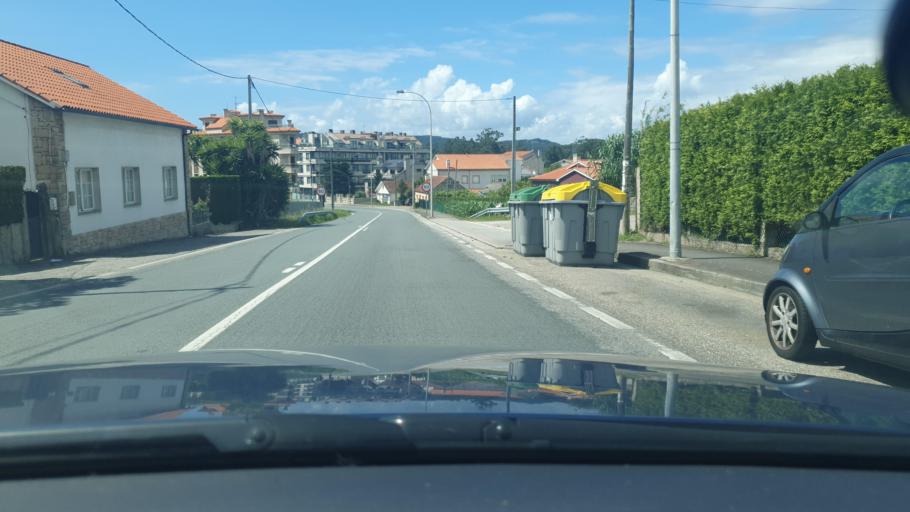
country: ES
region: Galicia
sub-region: Provincia de Pontevedra
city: O Grove
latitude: 42.4436
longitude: -8.8569
